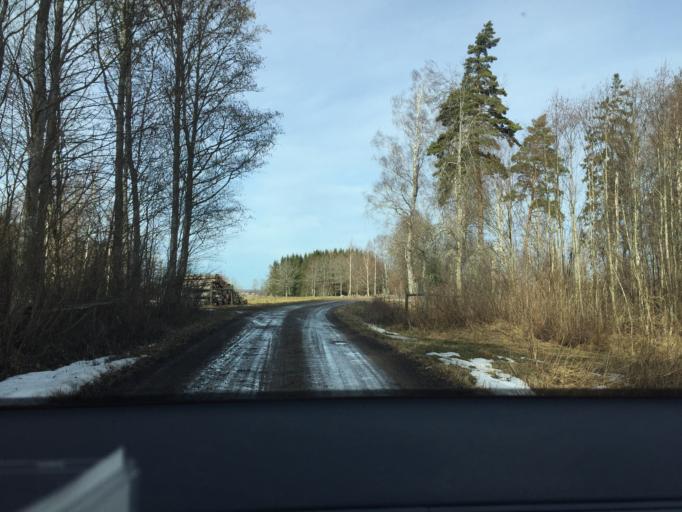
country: SE
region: OErebro
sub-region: Hallsbergs Kommun
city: Skollersta
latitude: 59.1197
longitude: 15.4366
